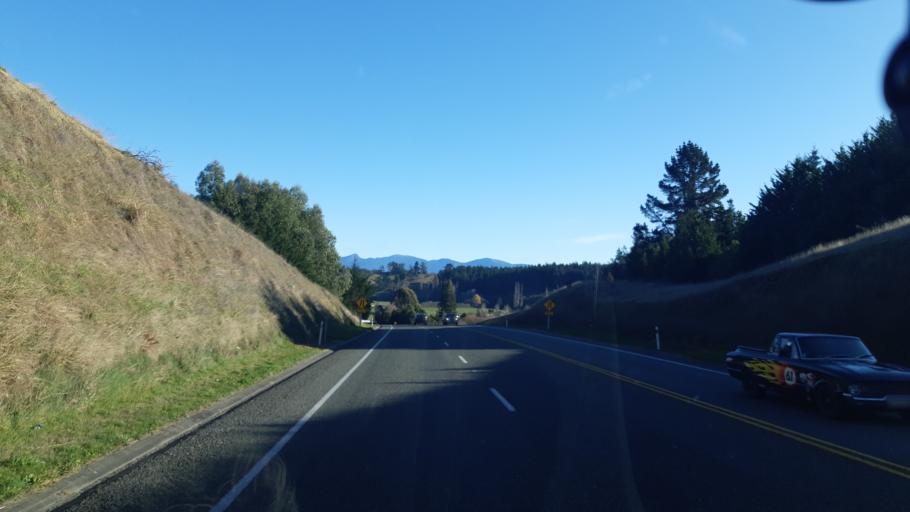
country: NZ
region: Tasman
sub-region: Tasman District
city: Mapua
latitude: -41.2840
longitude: 173.0769
